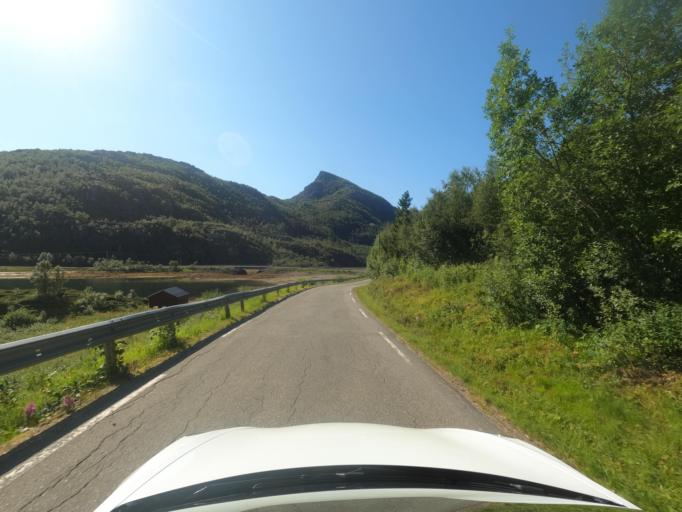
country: NO
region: Nordland
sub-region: Hadsel
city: Stokmarknes
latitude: 68.3016
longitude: 15.0412
